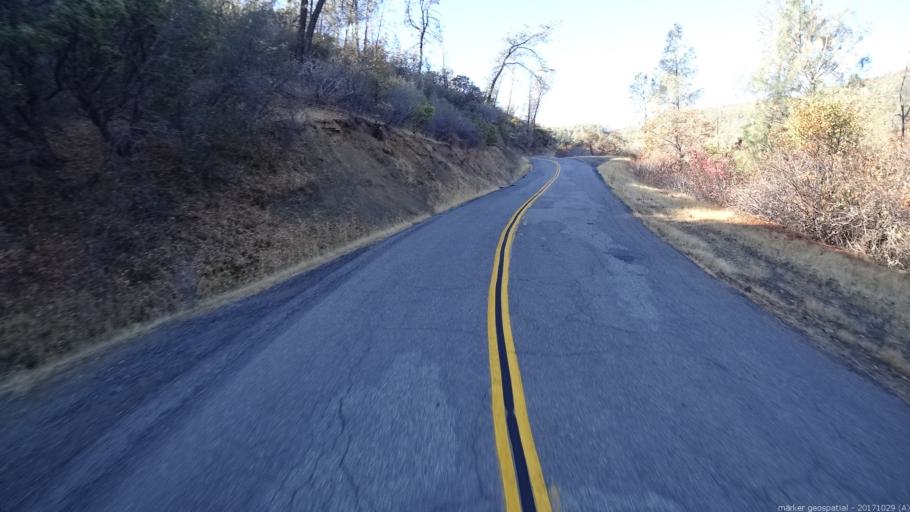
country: US
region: California
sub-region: Trinity County
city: Lewiston
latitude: 40.3880
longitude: -122.8218
